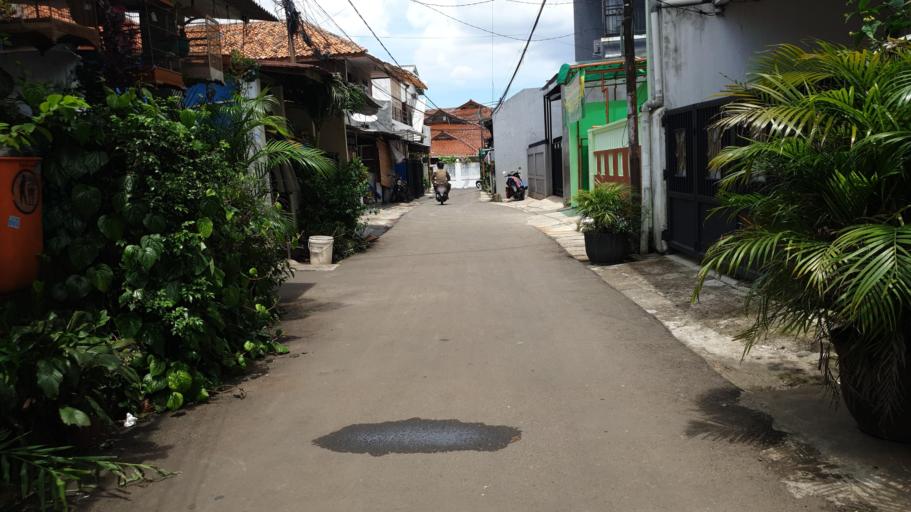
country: ID
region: Banten
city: South Tangerang
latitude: -6.2669
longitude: 106.7904
